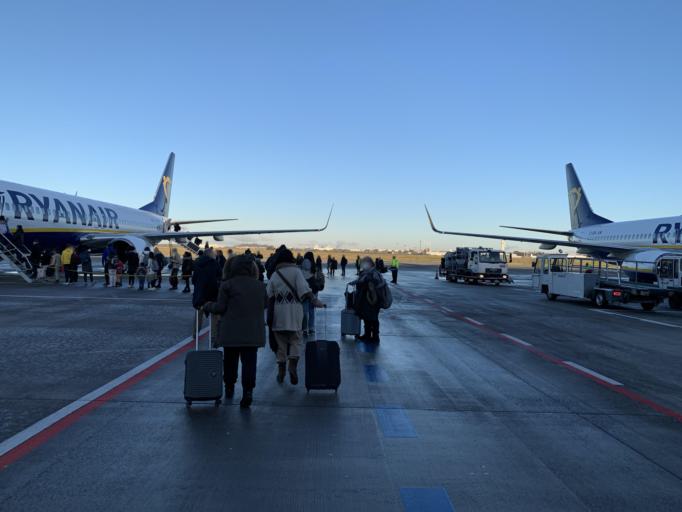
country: DE
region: Brandenburg
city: Schonefeld
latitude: 52.3679
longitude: 13.5091
